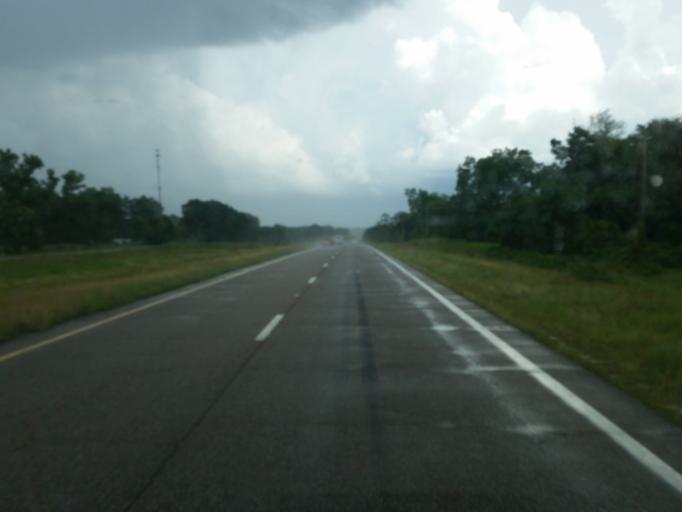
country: US
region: Mississippi
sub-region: George County
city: Lucedale
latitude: 30.9054
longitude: -88.4716
